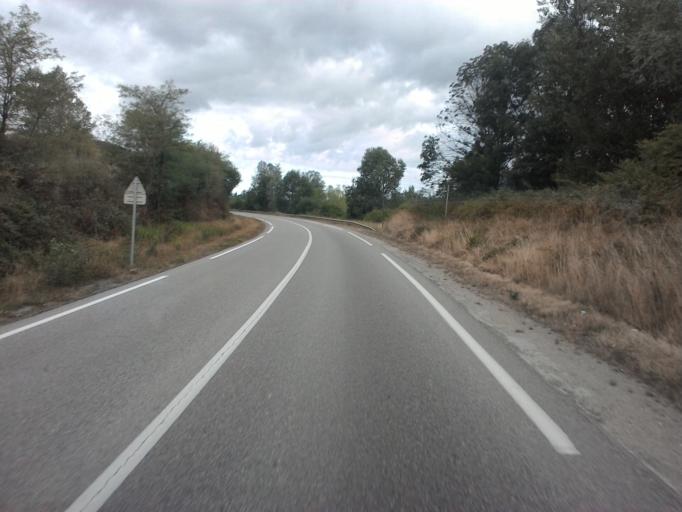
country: FR
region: Rhone-Alpes
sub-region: Departement de l'Ain
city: Sault-Brenaz
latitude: 45.8556
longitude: 5.4022
